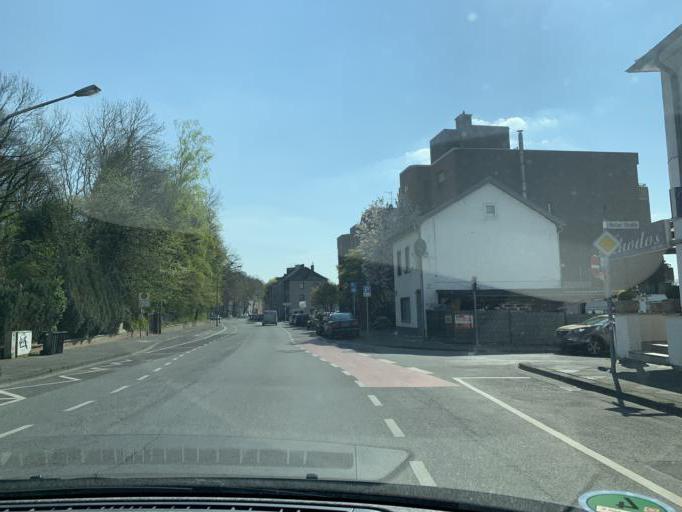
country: DE
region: North Rhine-Westphalia
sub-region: Regierungsbezirk Dusseldorf
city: Monchengladbach
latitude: 51.1429
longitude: 6.4560
